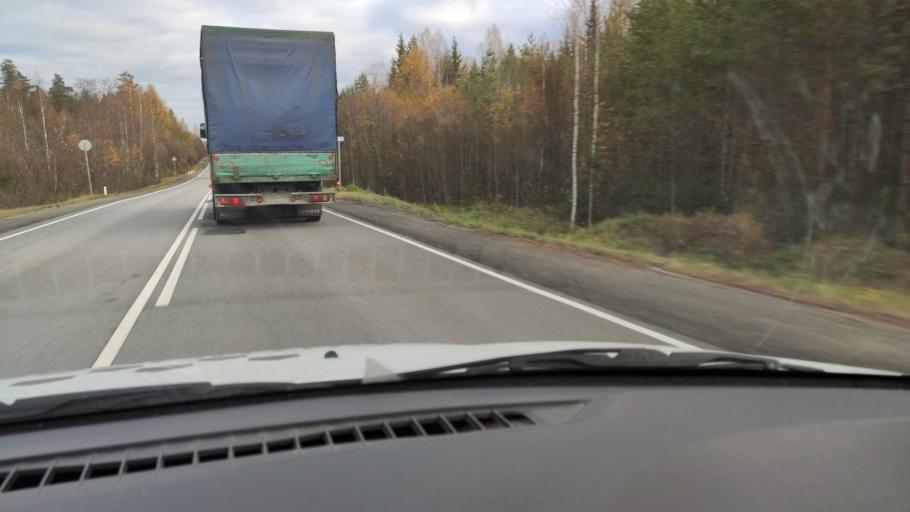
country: RU
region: Kirov
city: Dubrovka
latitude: 58.9081
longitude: 51.2491
